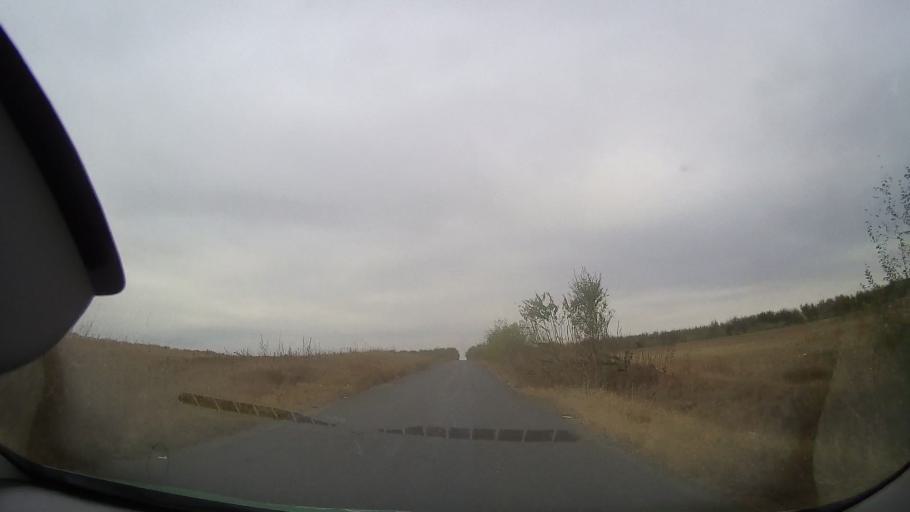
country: RO
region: Buzau
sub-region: Comuna Largu
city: Largu
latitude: 44.9721
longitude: 27.1750
